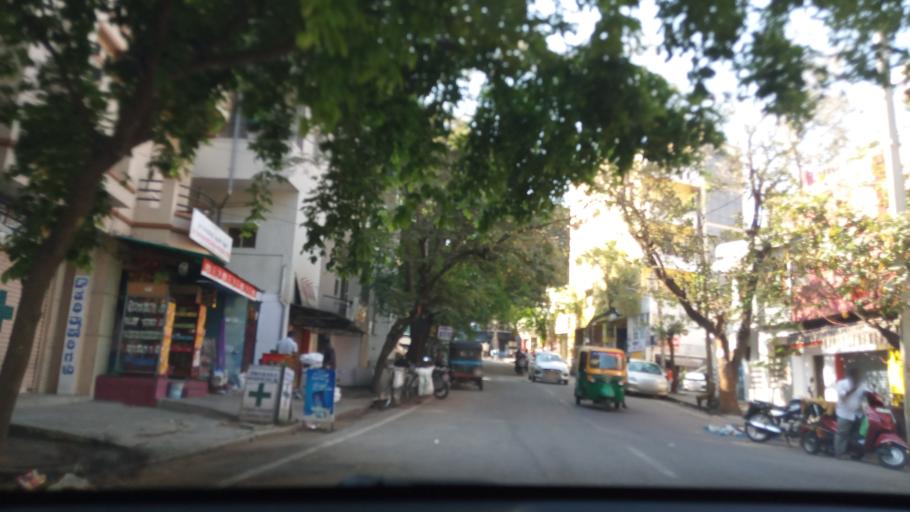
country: IN
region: Karnataka
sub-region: Bangalore Urban
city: Bangalore
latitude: 13.0122
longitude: 77.5451
